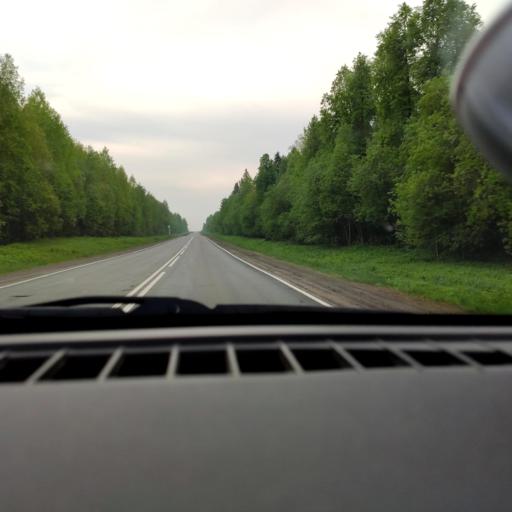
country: RU
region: Perm
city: Perm
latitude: 58.1863
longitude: 56.2195
